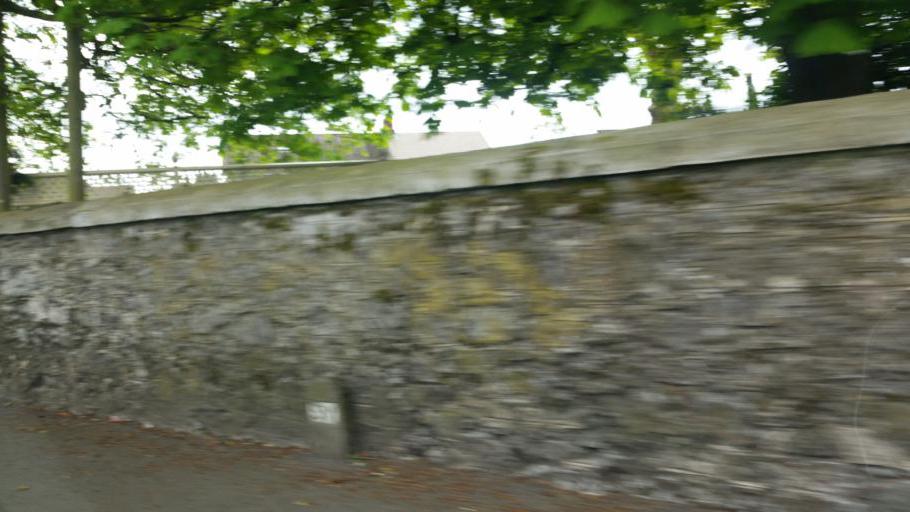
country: IE
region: Leinster
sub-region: Laois
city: Portlaoise
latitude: 53.0381
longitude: -7.3065
